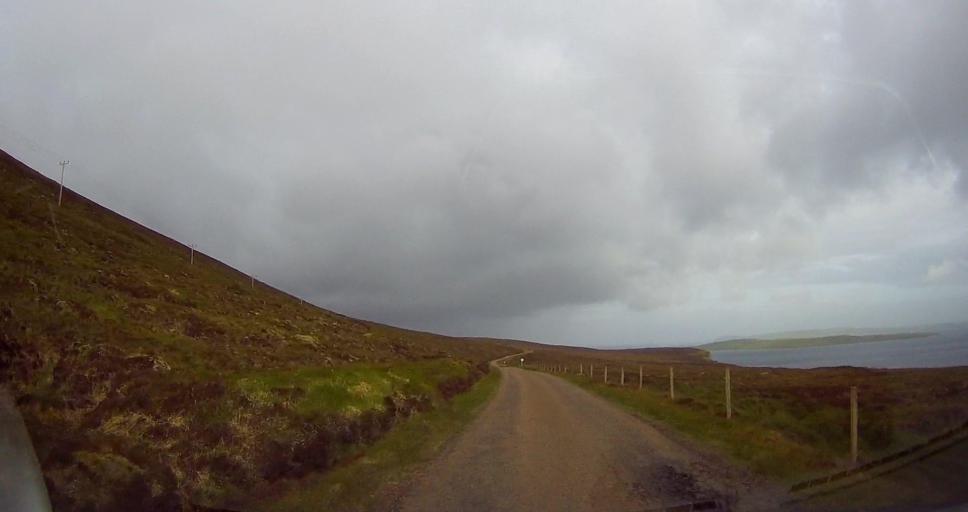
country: GB
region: Scotland
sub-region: Orkney Islands
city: Stromness
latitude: 58.8895
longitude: -3.2557
